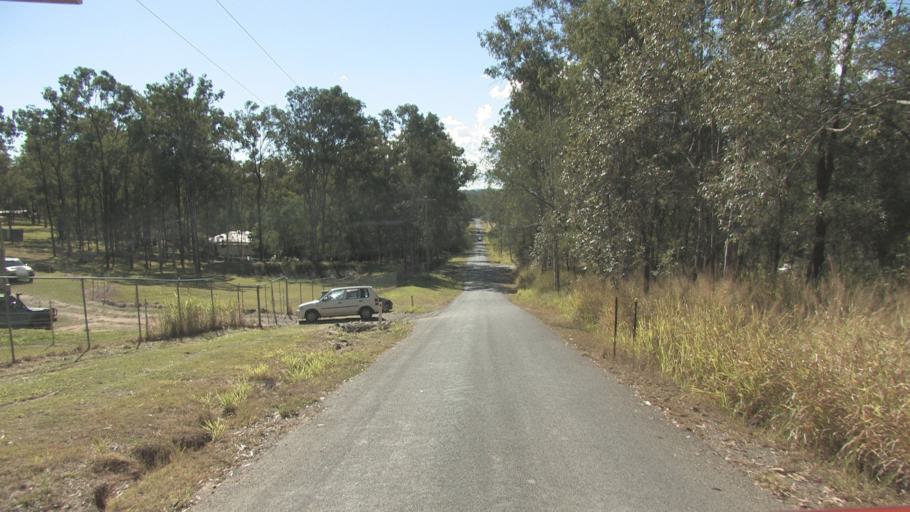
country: AU
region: Queensland
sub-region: Logan
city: Chambers Flat
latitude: -27.8104
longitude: 153.0819
